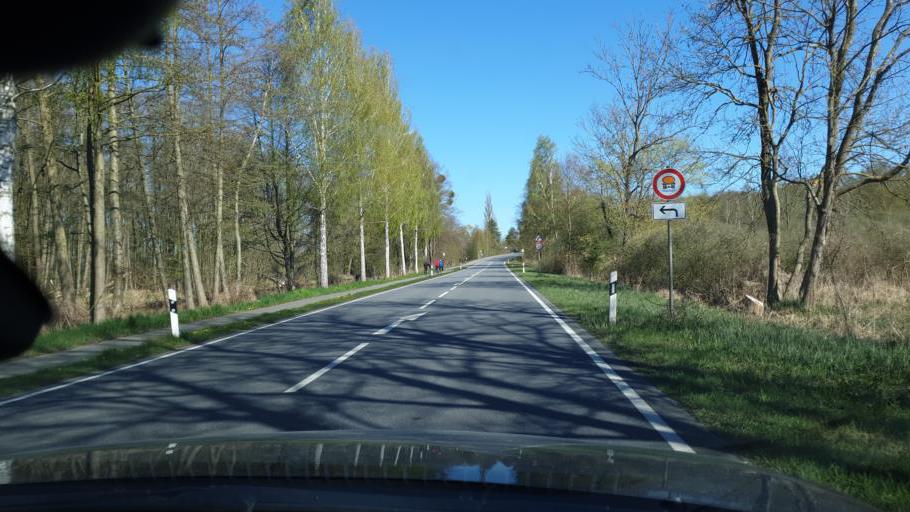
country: DE
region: Mecklenburg-Vorpommern
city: Seehof
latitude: 53.6745
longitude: 11.4494
